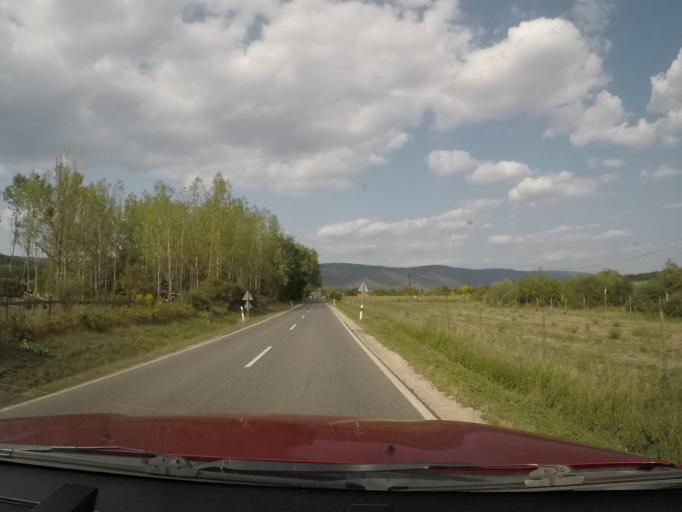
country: HU
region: Borsod-Abauj-Zemplen
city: Szendro
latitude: 48.5291
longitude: 20.7303
